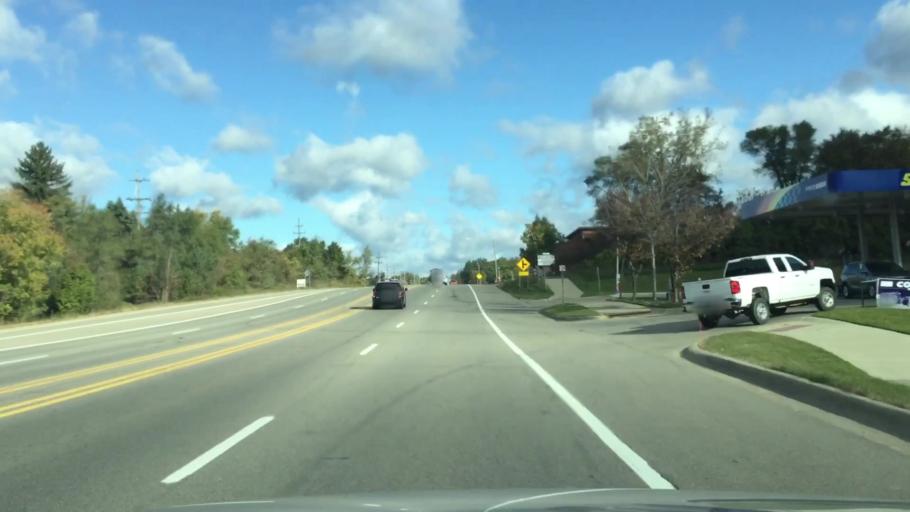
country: US
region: Michigan
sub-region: Oakland County
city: Clarkston
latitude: 42.7497
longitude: -83.4196
